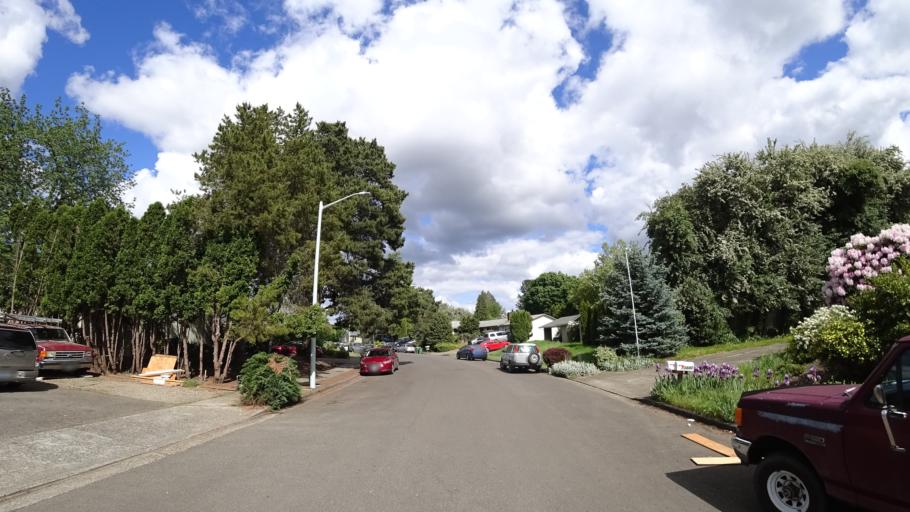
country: US
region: Oregon
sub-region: Washington County
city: Beaverton
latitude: 45.4812
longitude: -122.8197
